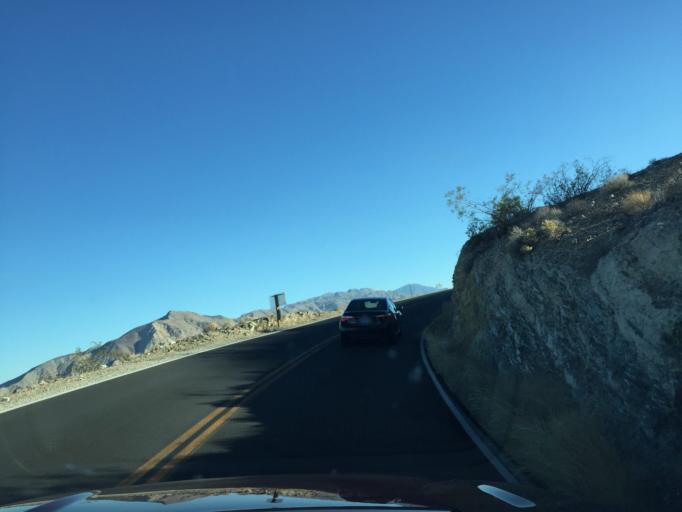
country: US
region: California
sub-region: Inyo County
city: Lone Pine
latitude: 36.3511
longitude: -117.5353
